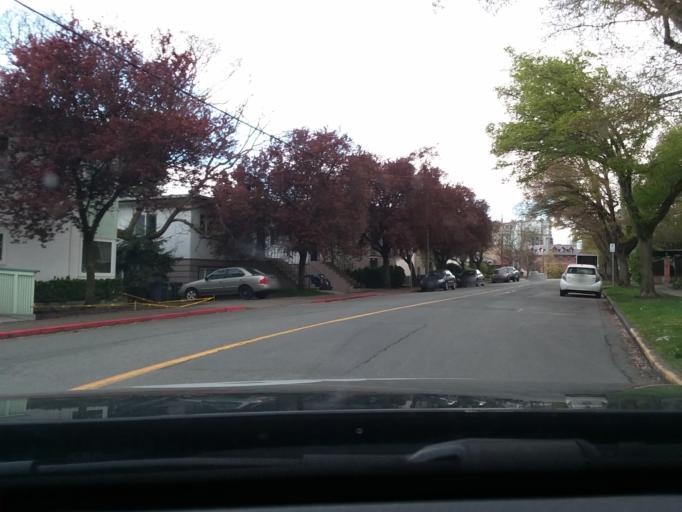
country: CA
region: British Columbia
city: Victoria
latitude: 48.4184
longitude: -123.3585
